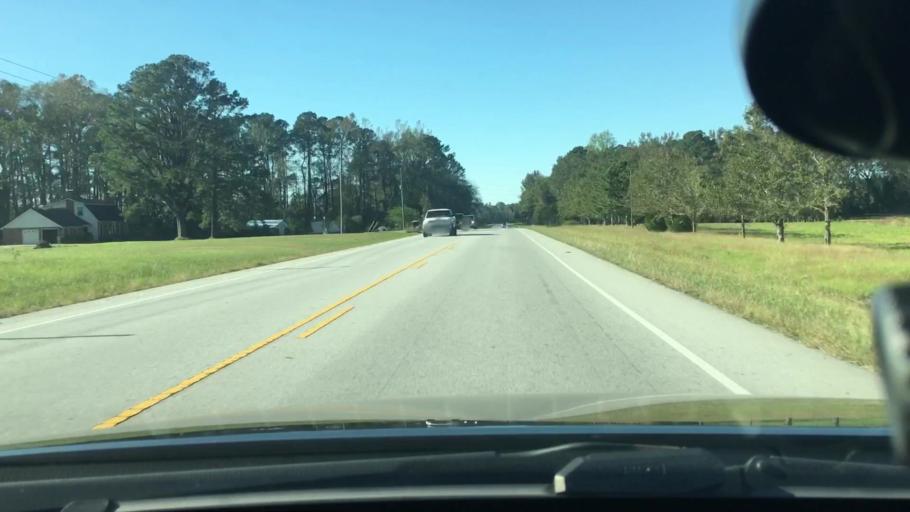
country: US
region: North Carolina
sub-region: Craven County
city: Trent Woods
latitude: 35.1670
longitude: -77.1229
